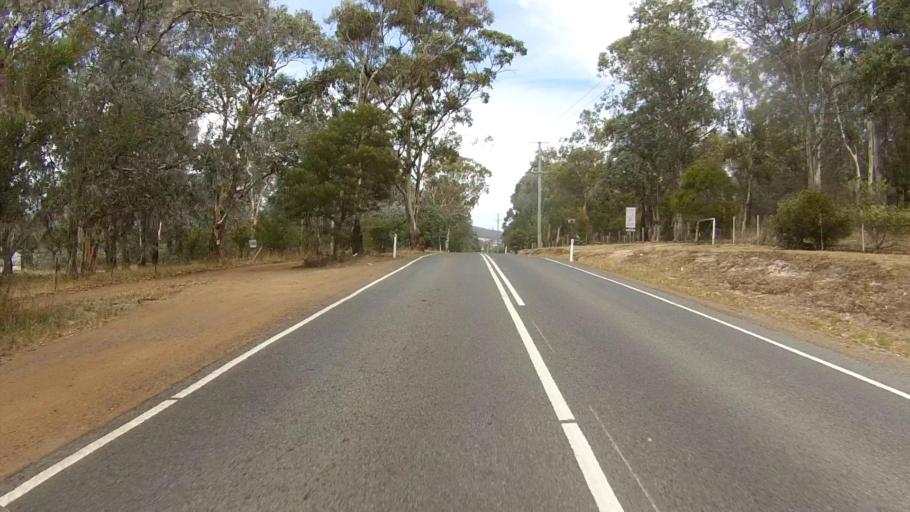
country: AU
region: Tasmania
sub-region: Clarence
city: Lauderdale
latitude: -42.8975
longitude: 147.4806
